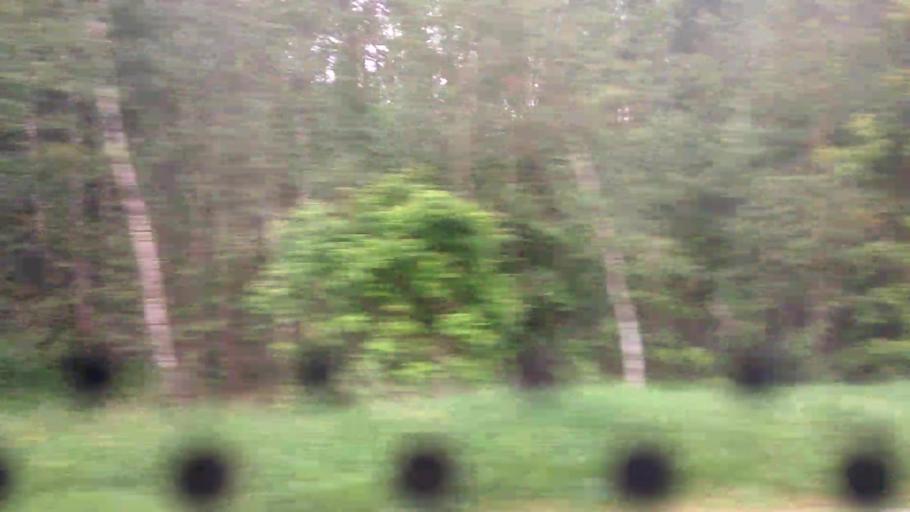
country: RU
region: Moskovskaya
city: Kolomna
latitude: 55.0518
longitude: 38.8715
